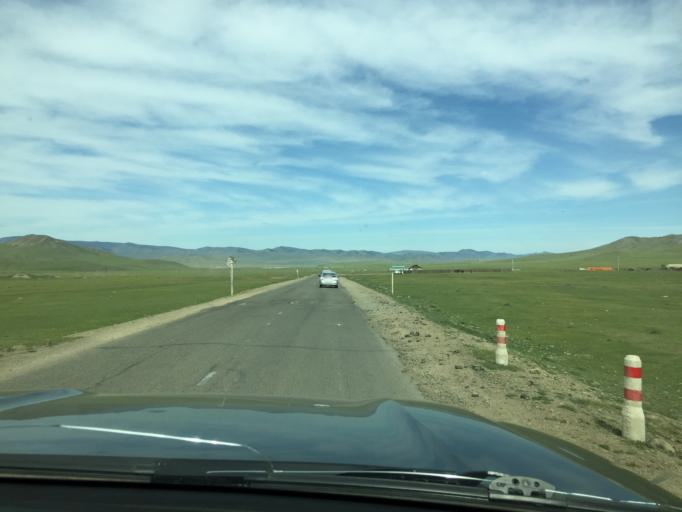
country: MN
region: Central Aimak
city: Ihsueuej
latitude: 48.2296
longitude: 106.2842
